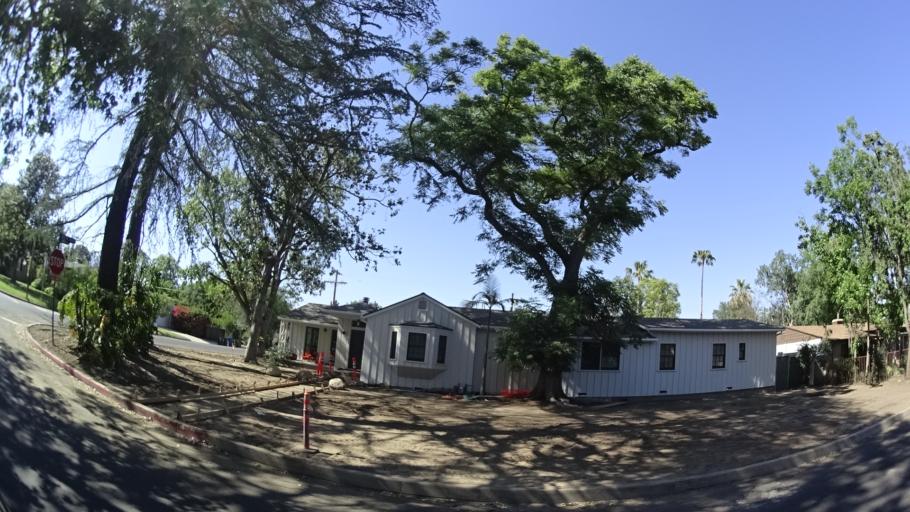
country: US
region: California
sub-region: Los Angeles County
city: North Hollywood
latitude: 34.1622
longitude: -118.3942
